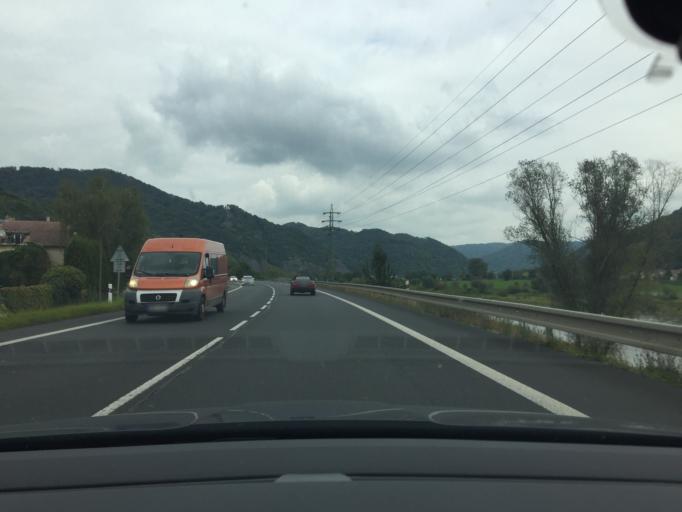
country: CZ
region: Ustecky
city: Povrly
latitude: 50.6716
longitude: 14.1637
